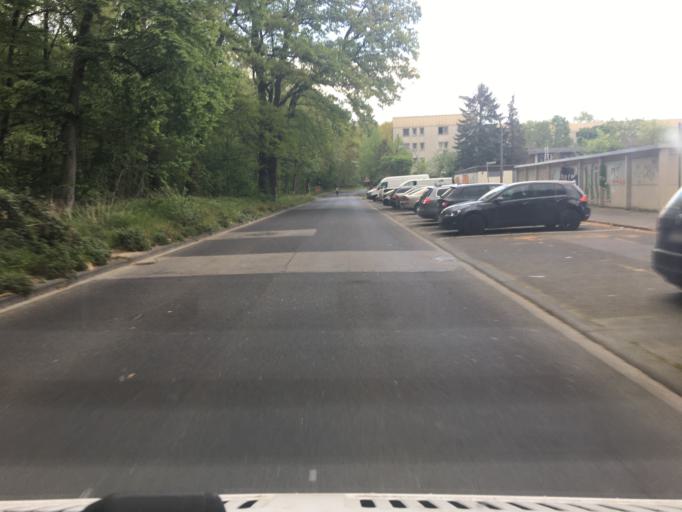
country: DE
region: North Rhine-Westphalia
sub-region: Regierungsbezirk Koln
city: Mengenich
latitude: 50.9841
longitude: 6.8678
